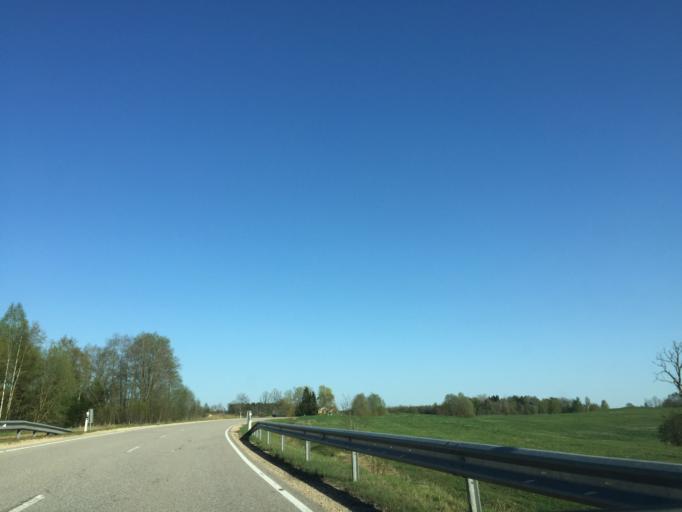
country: LV
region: Ergli
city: Ergli
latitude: 56.9015
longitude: 25.4625
